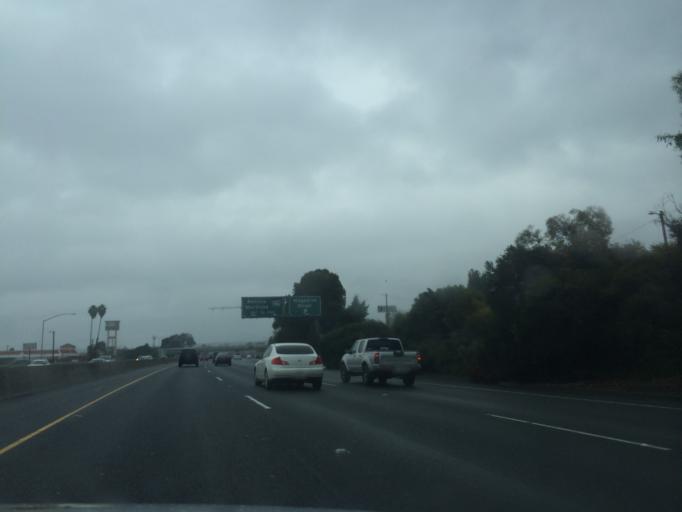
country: US
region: California
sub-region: Solano County
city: Vallejo
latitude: 38.0818
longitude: -122.2333
